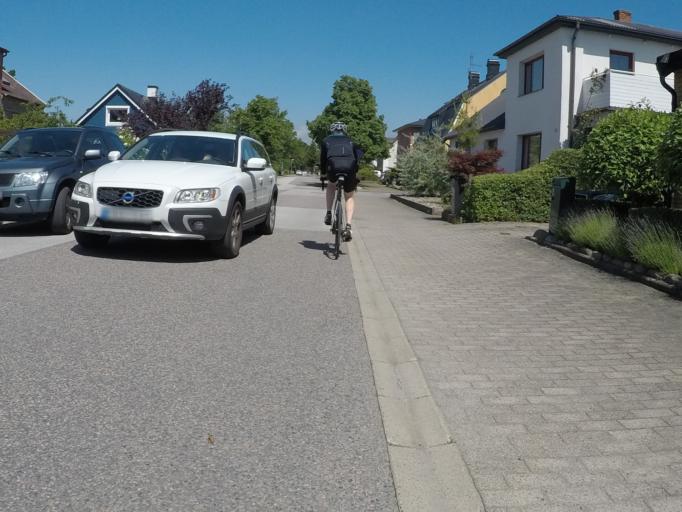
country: SE
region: Skane
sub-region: Lomma Kommun
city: Lomma
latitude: 55.6639
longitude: 13.0633
